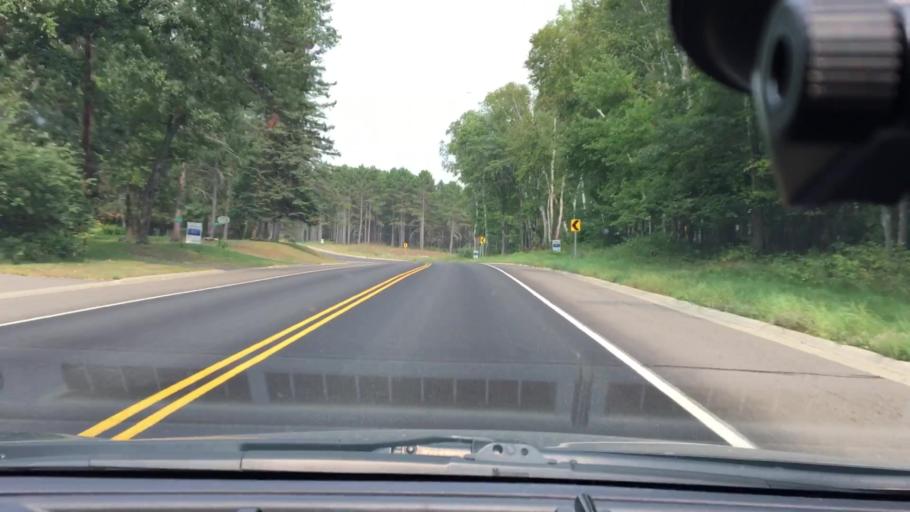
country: US
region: Minnesota
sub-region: Crow Wing County
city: Cross Lake
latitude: 46.7029
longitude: -94.0599
